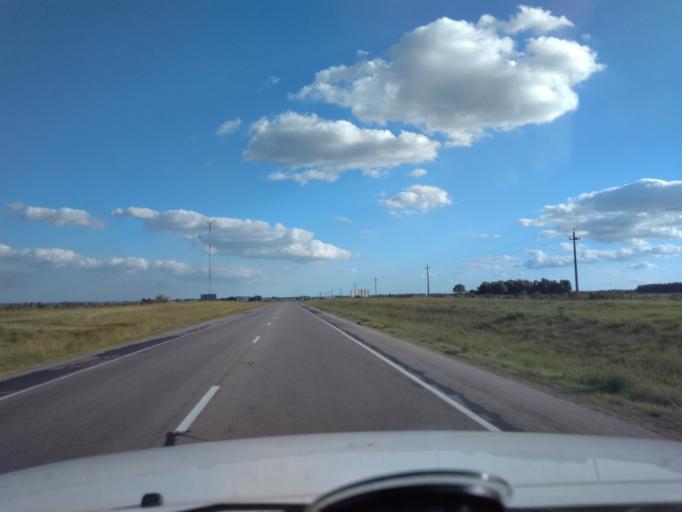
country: UY
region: Florida
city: Florida
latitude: -34.1954
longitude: -56.1987
